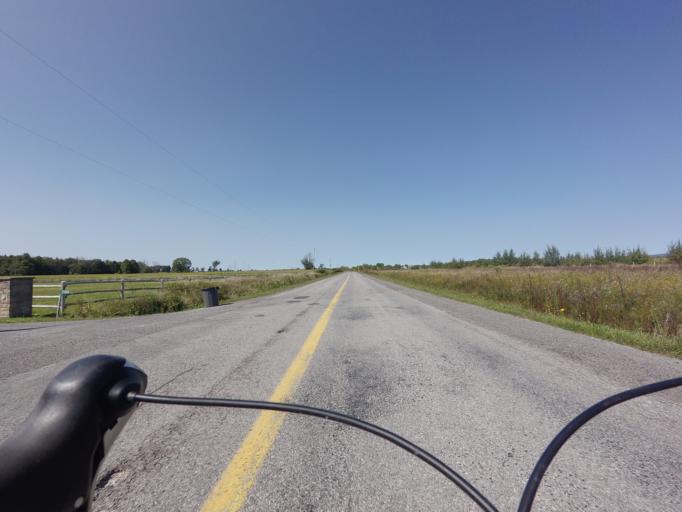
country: CA
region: Ontario
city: Arnprior
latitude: 45.4446
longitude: -76.0763
